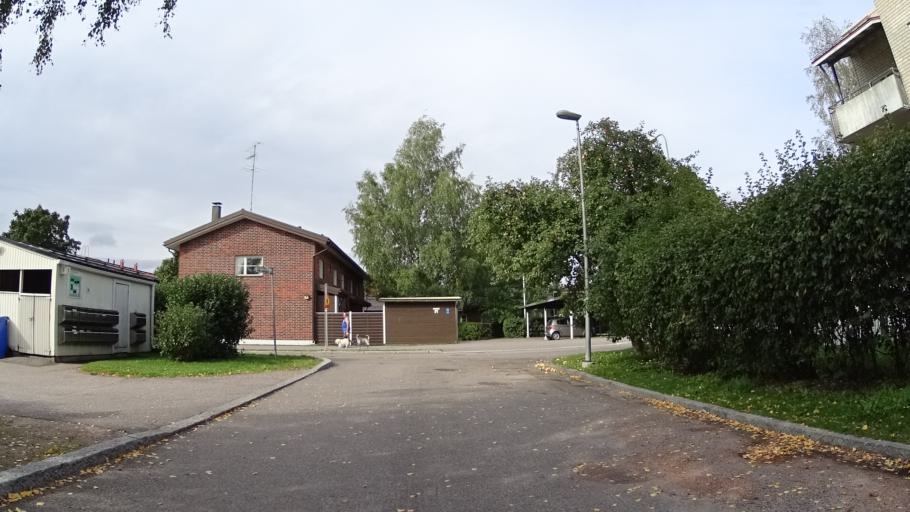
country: FI
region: Uusimaa
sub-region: Helsinki
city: Vantaa
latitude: 60.2931
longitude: 25.0197
